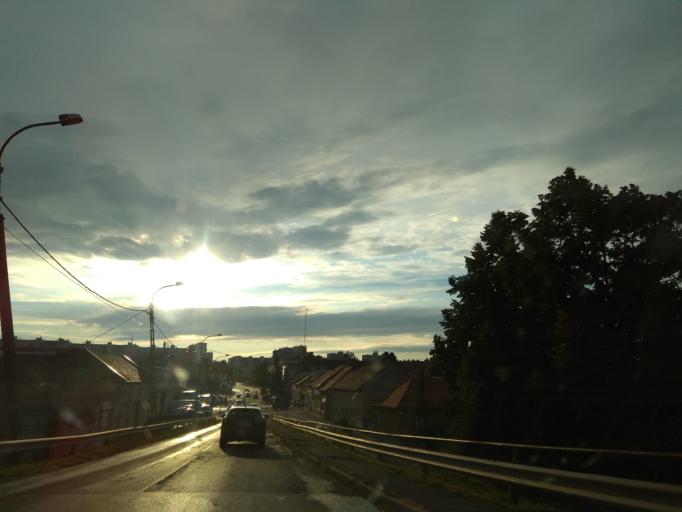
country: HU
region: Borsod-Abauj-Zemplen
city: Miskolc
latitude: 48.0987
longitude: 20.8011
